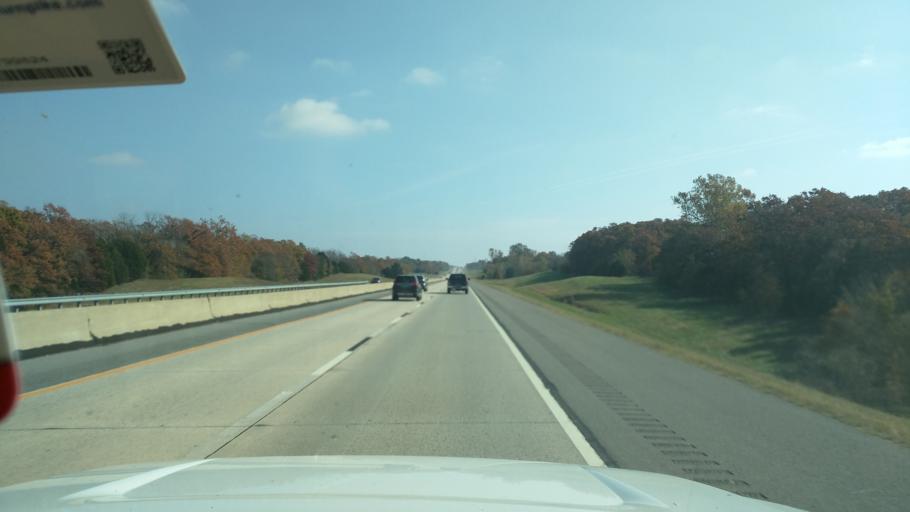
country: US
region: Oklahoma
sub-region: Muskogee County
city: Muskogee
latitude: 35.8371
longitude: -95.3797
